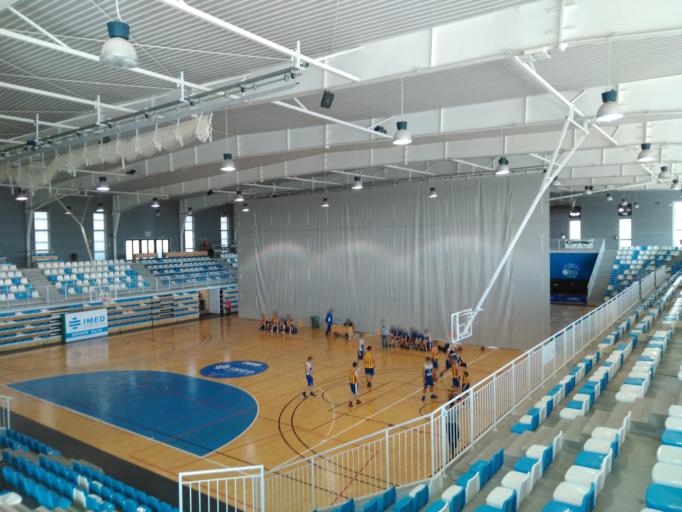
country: ES
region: Valencia
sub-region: Provincia de Alicante
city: Altea
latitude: 38.6059
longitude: -0.0442
